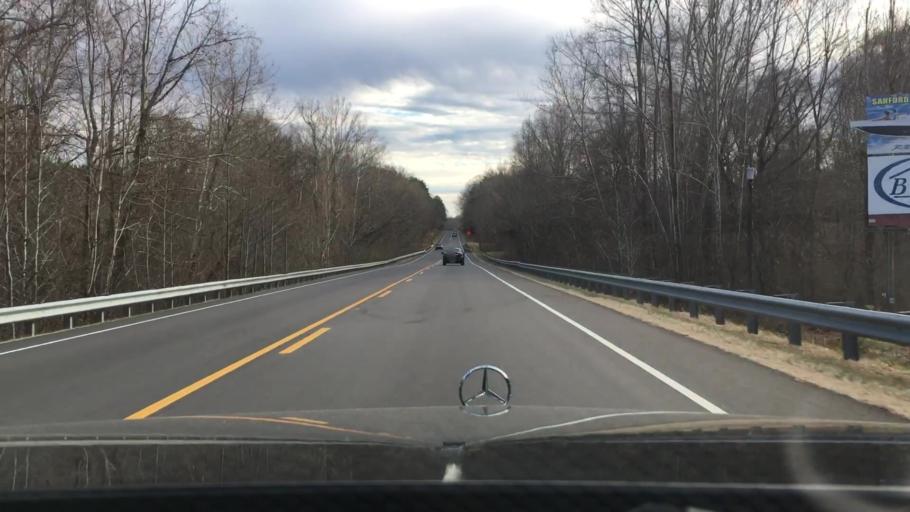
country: US
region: North Carolina
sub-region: Caswell County
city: Yanceyville
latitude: 36.4789
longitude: -79.3794
